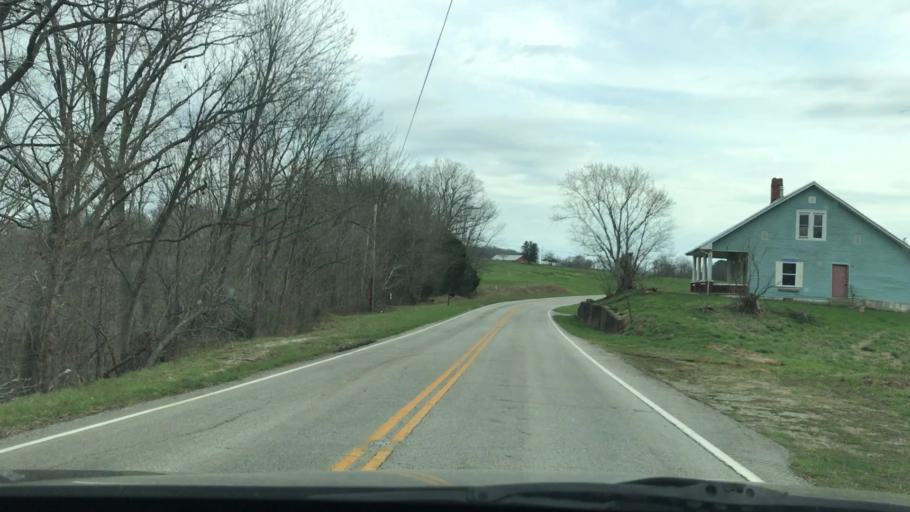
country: US
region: Kentucky
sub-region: Hart County
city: Munfordville
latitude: 37.3000
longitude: -85.7636
